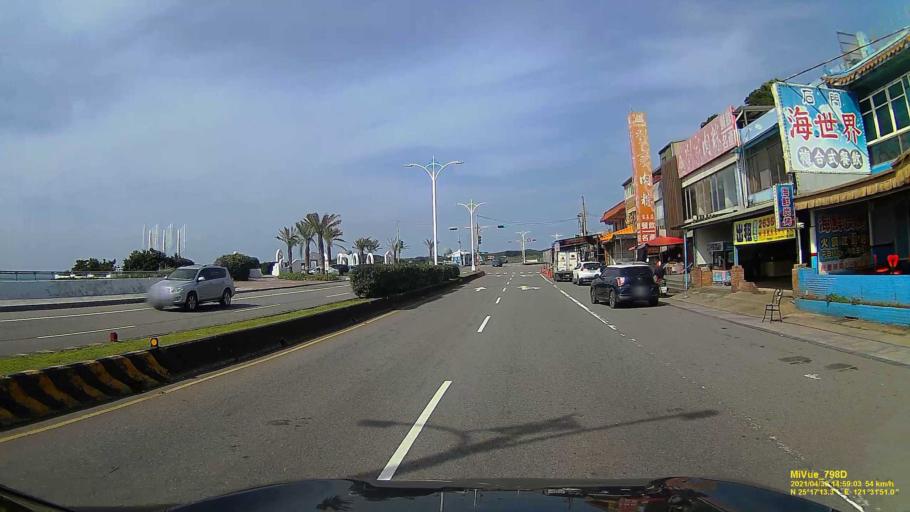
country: TW
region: Taipei
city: Taipei
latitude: 25.2872
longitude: 121.5310
